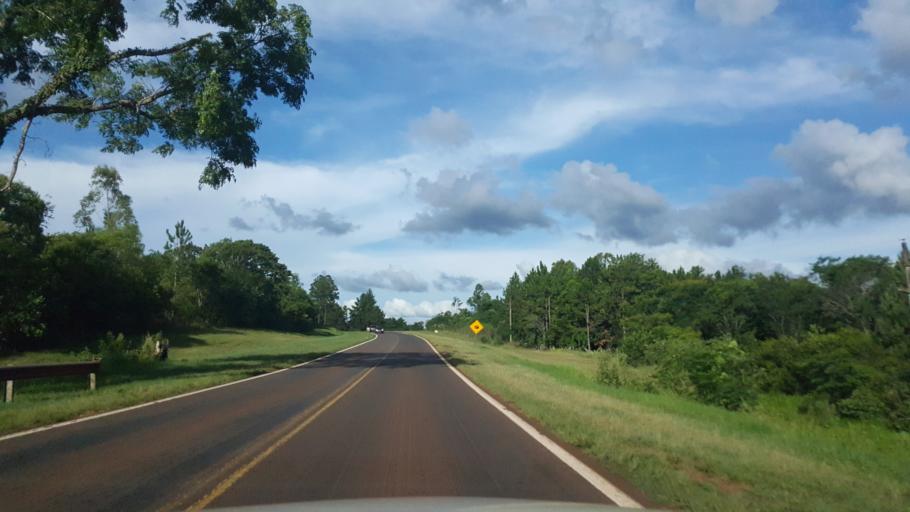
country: AR
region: Misiones
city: Santa Ana
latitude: -27.3688
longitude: -55.5624
